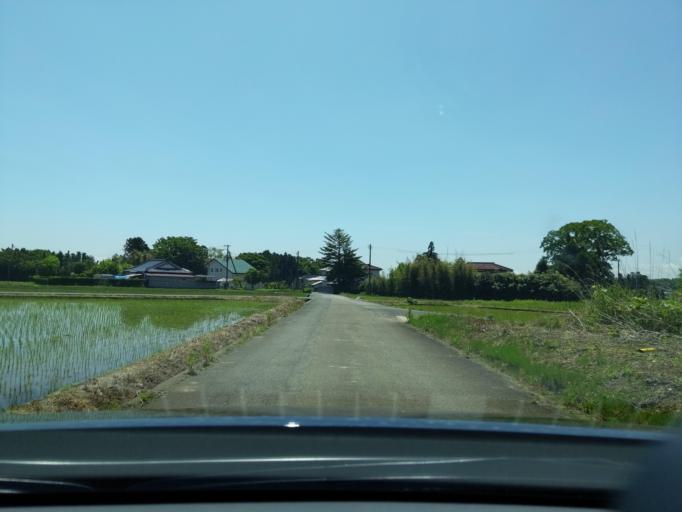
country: JP
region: Fukushima
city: Koriyama
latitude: 37.3910
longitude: 140.2889
